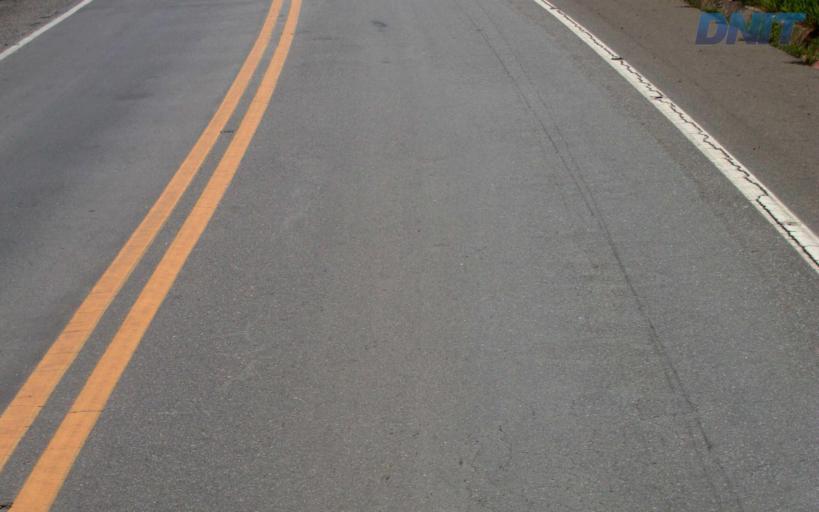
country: BR
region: Minas Gerais
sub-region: Governador Valadares
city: Governador Valadares
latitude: -19.0664
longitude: -42.1643
